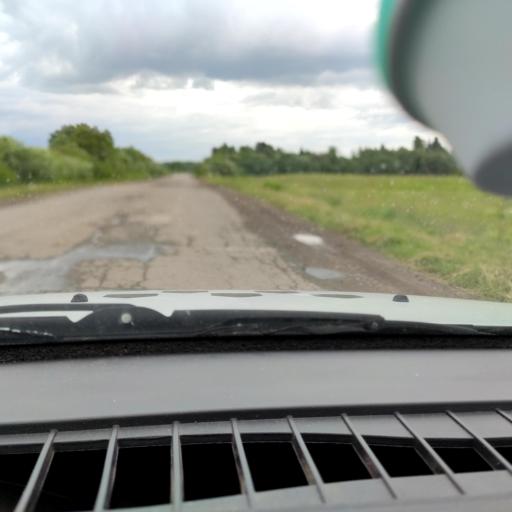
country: RU
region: Perm
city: Uinskoye
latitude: 57.1657
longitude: 56.5672
